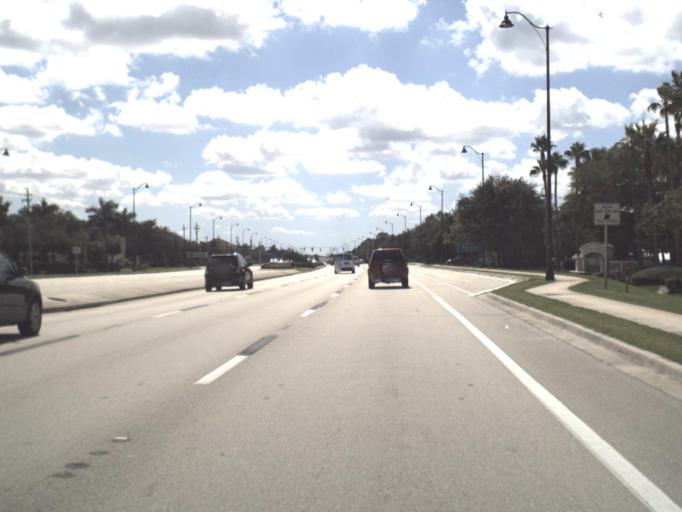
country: US
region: Florida
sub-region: Lee County
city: Bonita Springs
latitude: 26.3509
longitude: -81.8078
